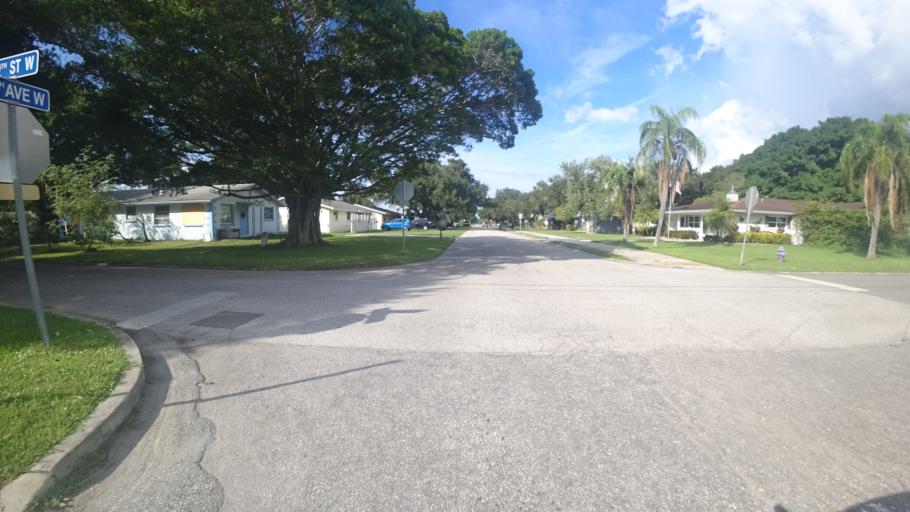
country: US
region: Florida
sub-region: Manatee County
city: Palmetto
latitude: 27.5231
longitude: -82.5934
